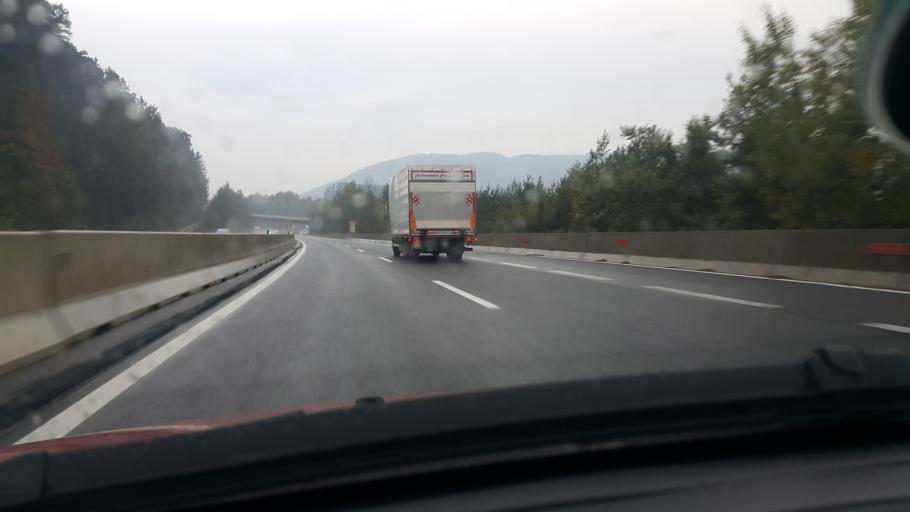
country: AT
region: Carinthia
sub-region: Politischer Bezirk Volkermarkt
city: Voelkermarkt
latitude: 46.6764
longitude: 14.5919
